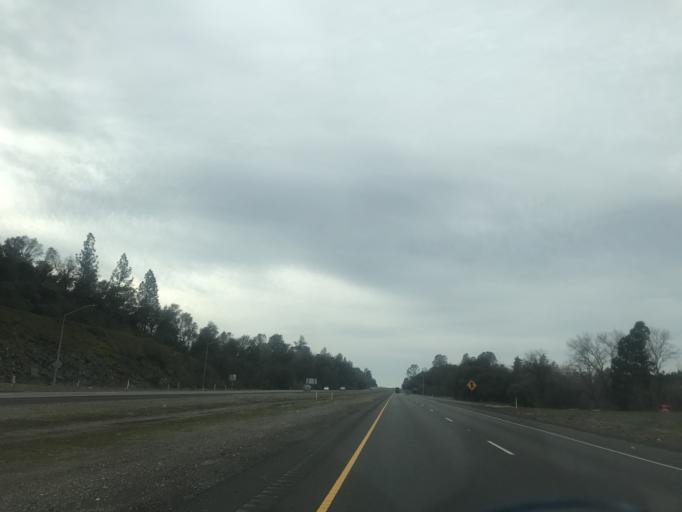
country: US
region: California
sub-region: El Dorado County
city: Deer Park
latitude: 38.7045
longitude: -120.8576
